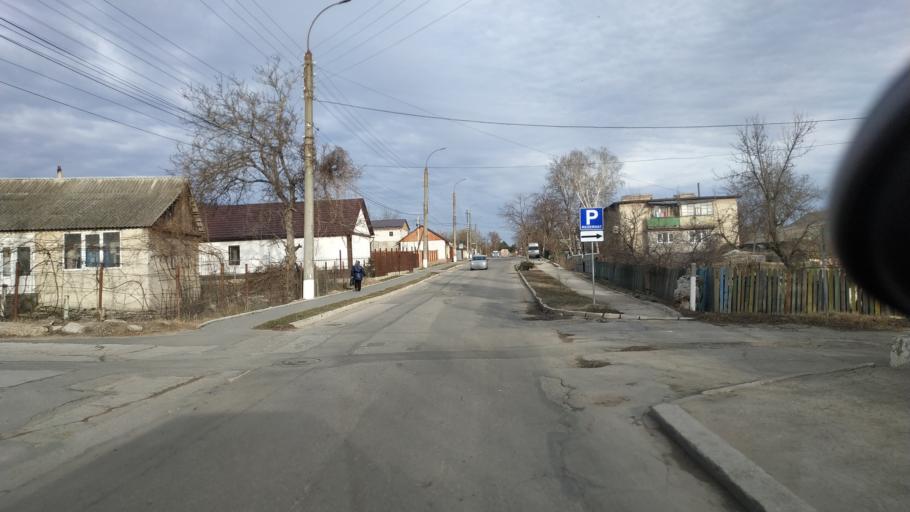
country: MD
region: Chisinau
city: Vadul lui Voda
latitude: 47.0919
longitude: 29.0756
